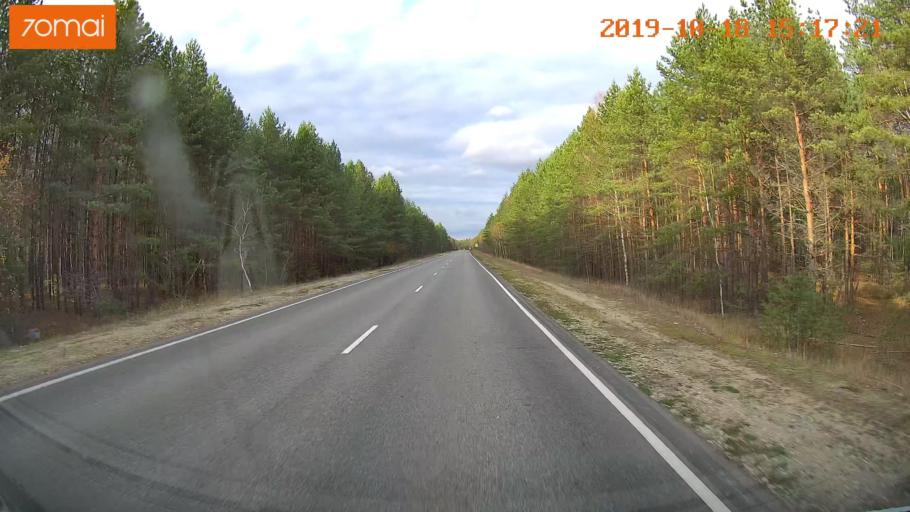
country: RU
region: Vladimir
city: Anopino
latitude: 55.6485
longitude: 40.7264
